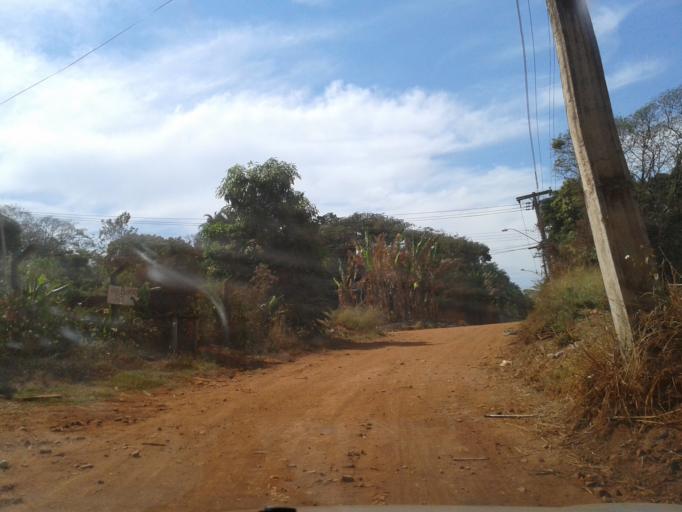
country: BR
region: Goias
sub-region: Goiania
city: Goiania
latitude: -16.6420
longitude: -49.3462
